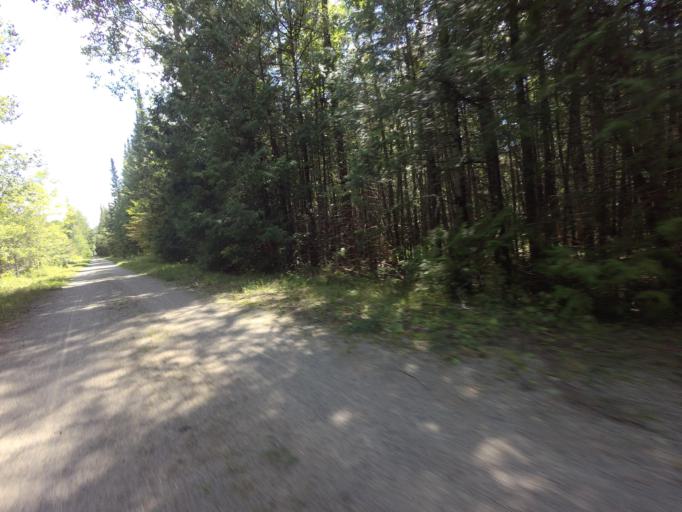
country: CA
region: Ontario
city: Orangeville
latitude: 43.7820
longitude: -80.2218
